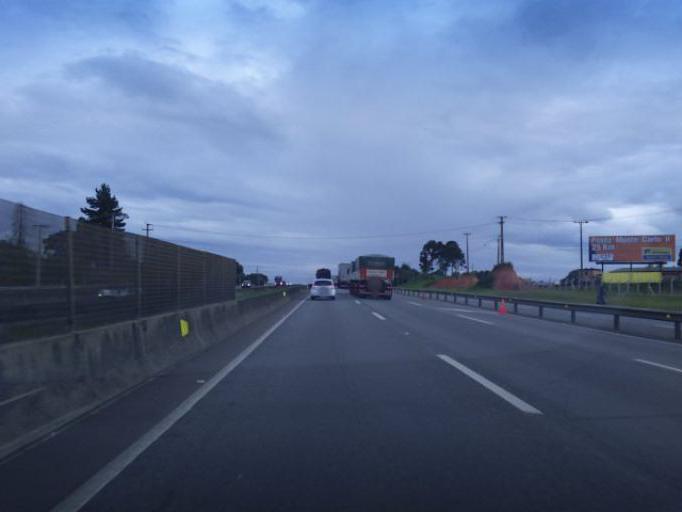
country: BR
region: Parana
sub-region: Sao Jose Dos Pinhais
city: Sao Jose dos Pinhais
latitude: -25.6184
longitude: -49.1688
